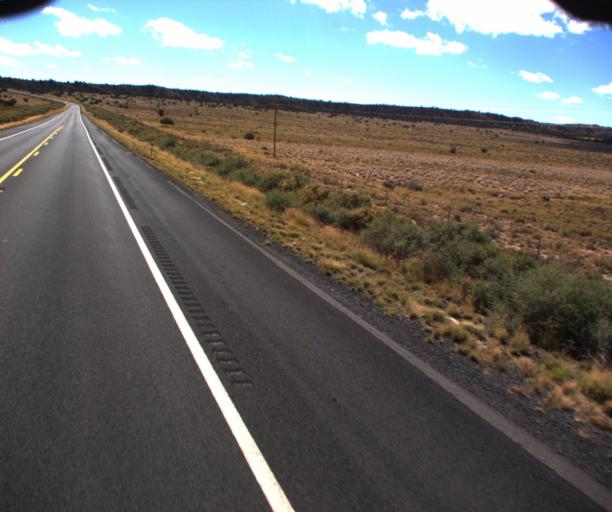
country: US
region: Arizona
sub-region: Apache County
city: Houck
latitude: 35.0444
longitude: -109.2709
